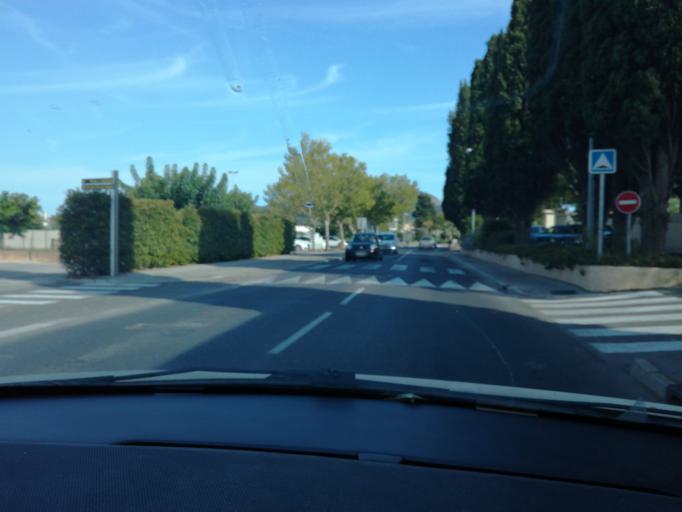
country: FR
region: Provence-Alpes-Cote d'Azur
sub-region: Departement du Var
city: La Crau
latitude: 43.1532
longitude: 6.0713
